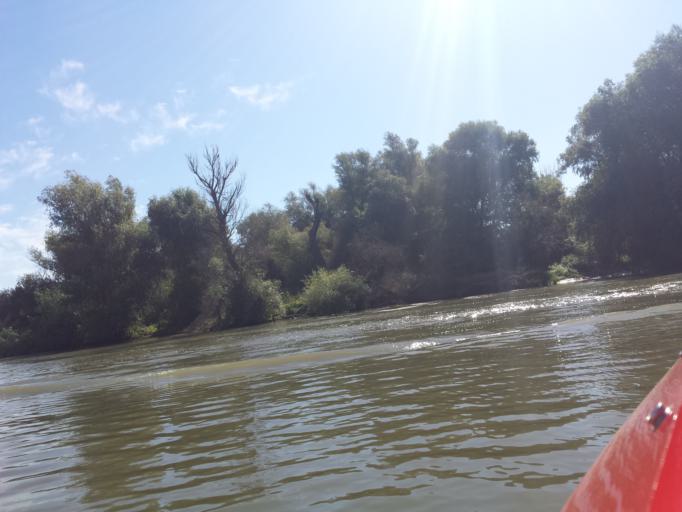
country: RO
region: Tulcea
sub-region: Comuna Pardina
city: Pardina
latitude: 45.2438
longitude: 29.0813
